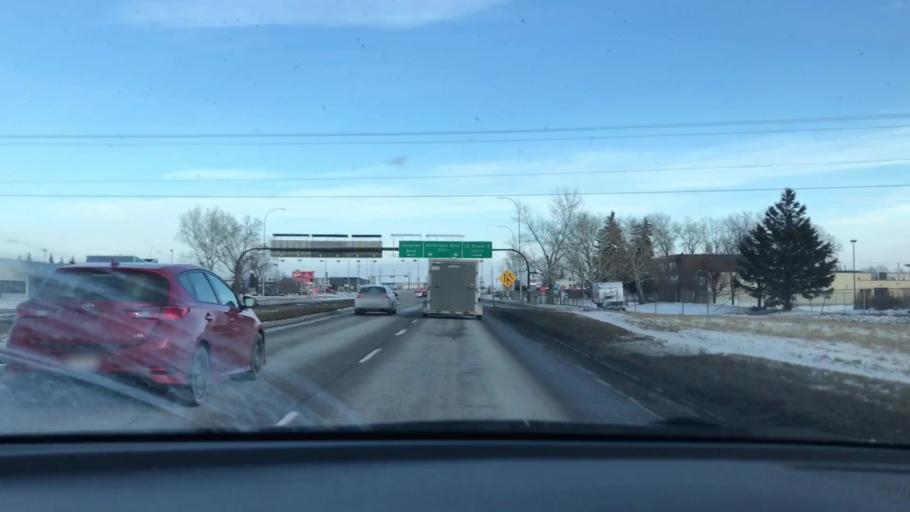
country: CA
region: Alberta
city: Calgary
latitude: 51.0960
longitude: -114.0373
